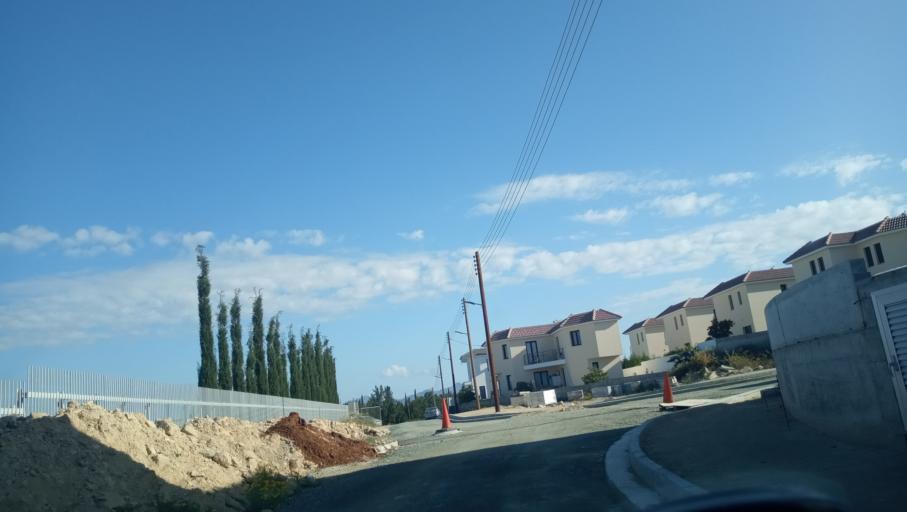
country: CY
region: Lefkosia
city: Geri
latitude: 35.1035
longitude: 33.4019
